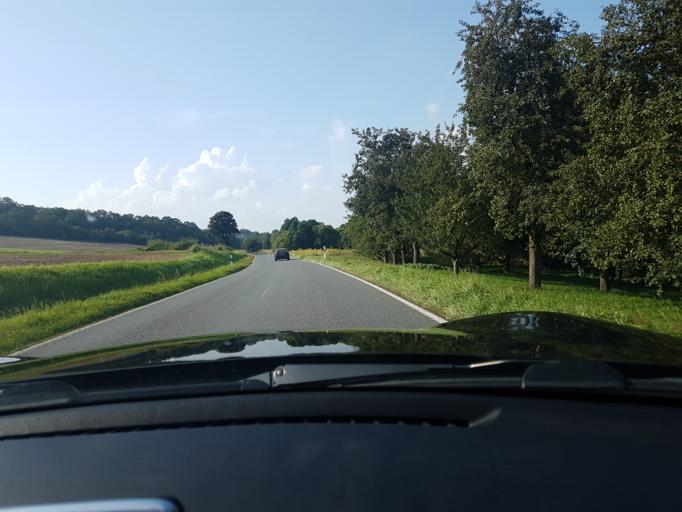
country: DE
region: Baden-Wuerttemberg
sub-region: Karlsruhe Region
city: Seckach
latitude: 49.4464
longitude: 9.3703
